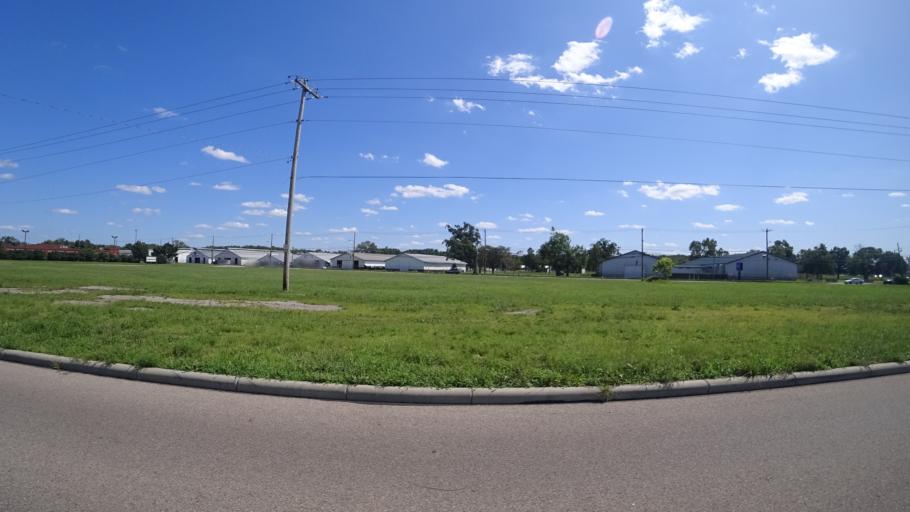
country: US
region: Ohio
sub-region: Butler County
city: Hamilton
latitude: 39.4030
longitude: -84.5393
